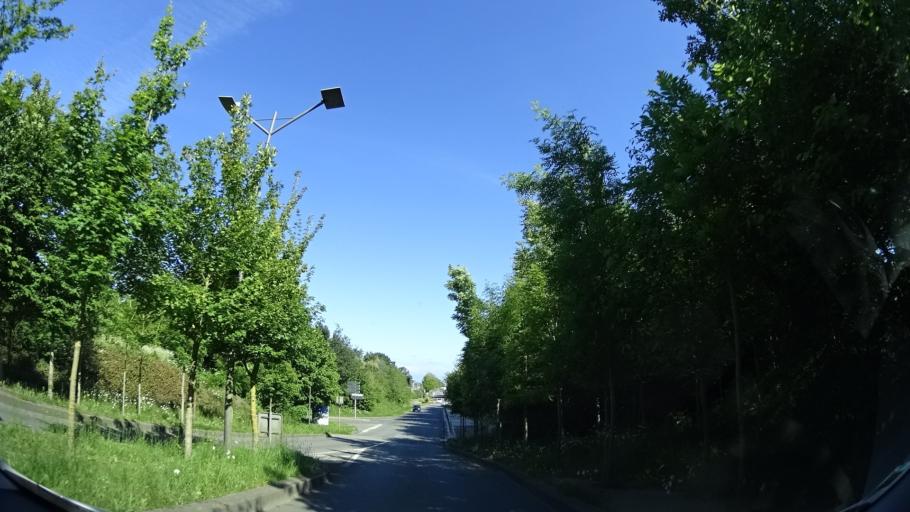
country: FR
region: Brittany
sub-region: Departement d'Ille-et-Vilaine
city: Saint-Jouan-des-Guerets
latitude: 48.6155
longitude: -1.9823
